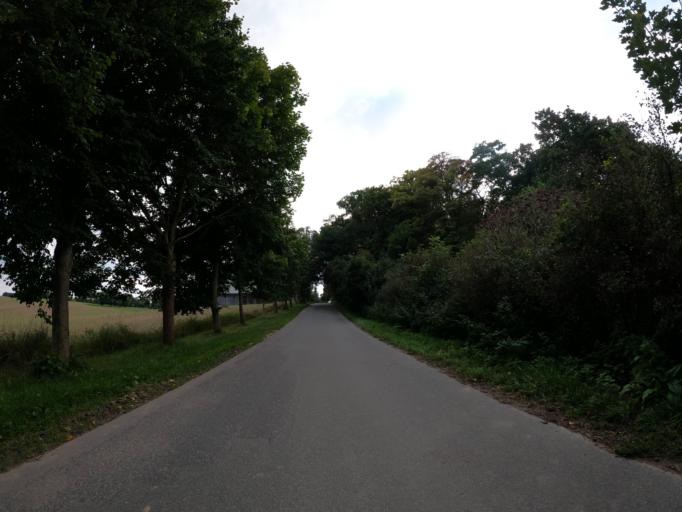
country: DE
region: Mecklenburg-Vorpommern
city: Robel
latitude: 53.4333
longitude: 12.5394
